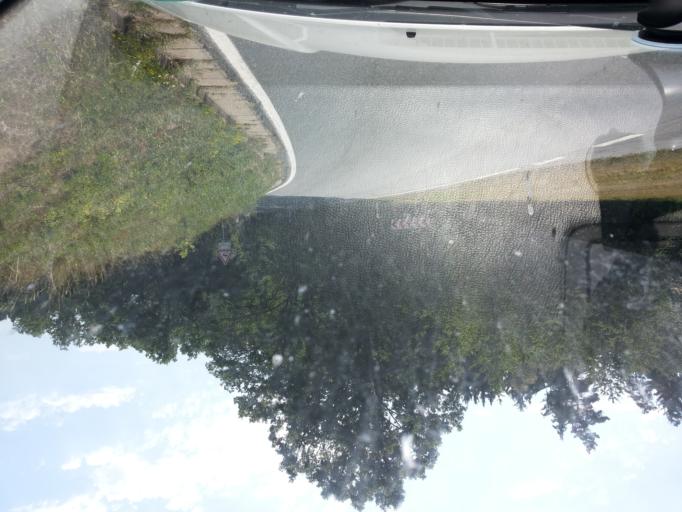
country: DE
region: Bavaria
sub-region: Regierungsbezirk Mittelfranken
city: Markt Erlbach
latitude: 49.5073
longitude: 10.6820
